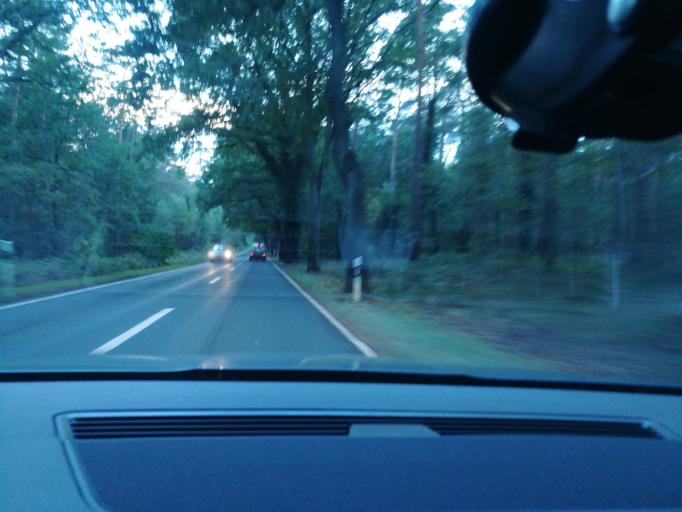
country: DE
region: Lower Saxony
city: Linsburg
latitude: 52.5351
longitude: 9.3716
